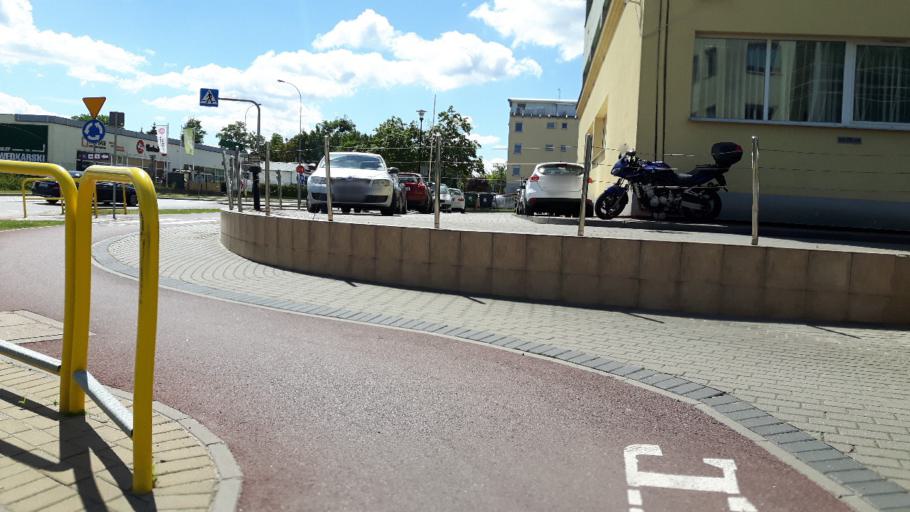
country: PL
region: Pomeranian Voivodeship
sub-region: Gdynia
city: Gdynia
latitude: 54.4967
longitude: 18.5344
